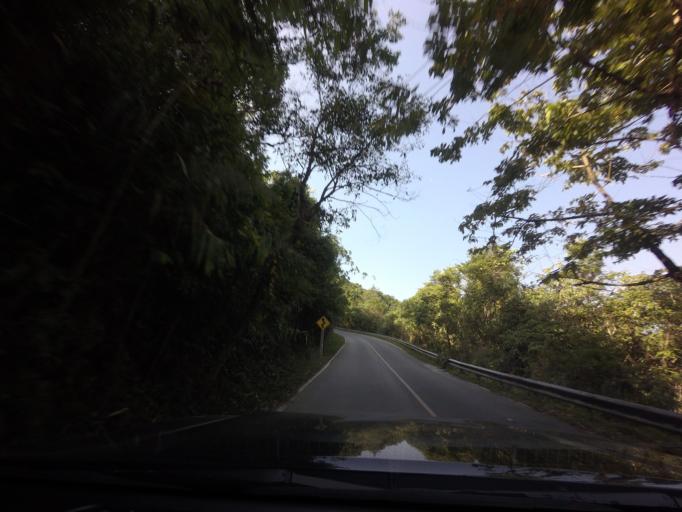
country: TH
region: Kanchanaburi
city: Thong Pha Phum
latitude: 14.6779
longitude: 98.3721
